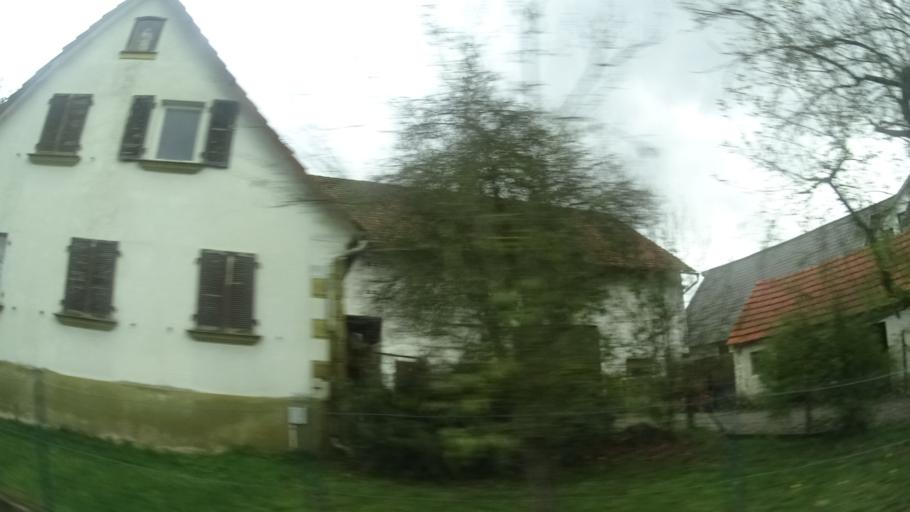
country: DE
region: Bavaria
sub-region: Regierungsbezirk Unterfranken
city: Oberelsbach
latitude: 50.3831
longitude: 10.1023
